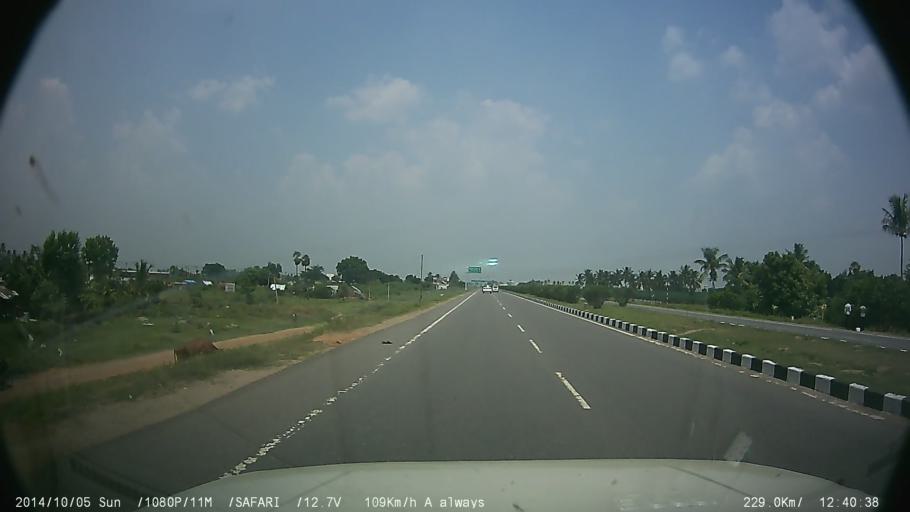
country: IN
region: Tamil Nadu
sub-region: Cuddalore
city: Vriddhachalam
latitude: 11.6970
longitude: 79.3162
